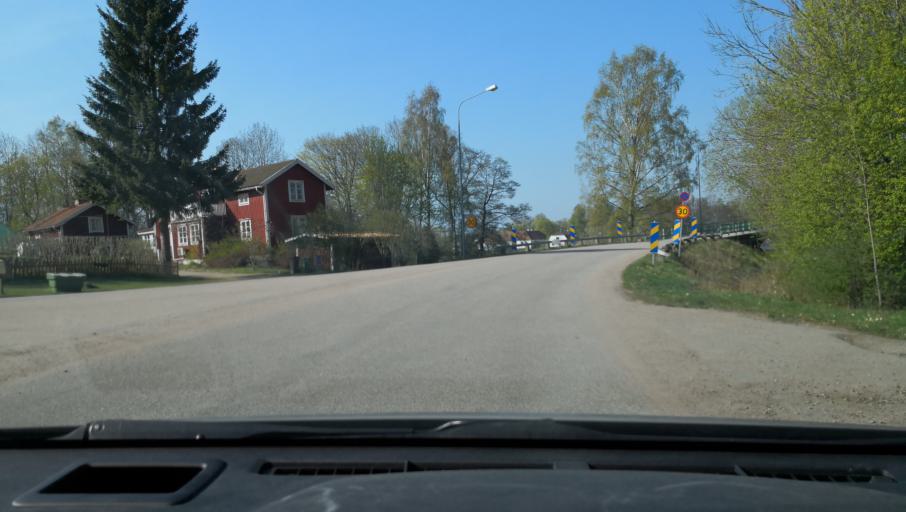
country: SE
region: Uppsala
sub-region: Heby Kommun
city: Tarnsjo
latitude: 60.2830
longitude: 16.8834
